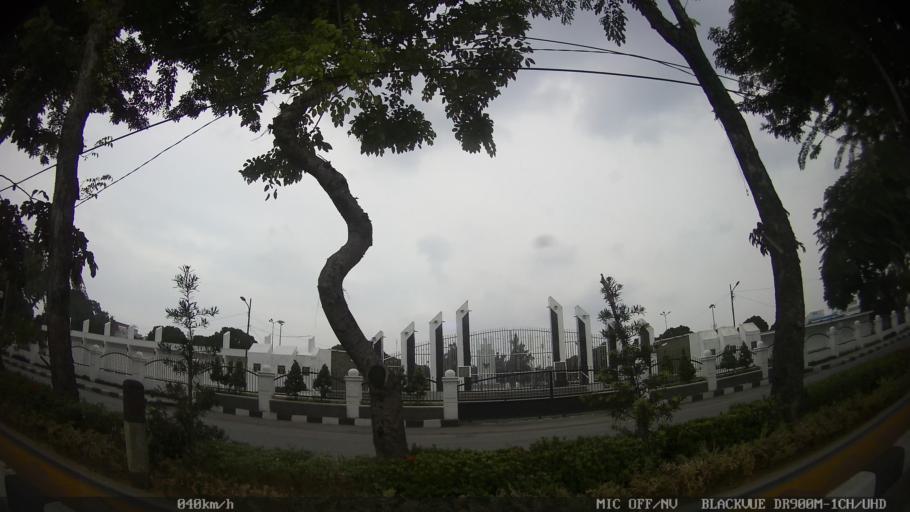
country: ID
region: North Sumatra
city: Medan
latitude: 3.5696
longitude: 98.6906
